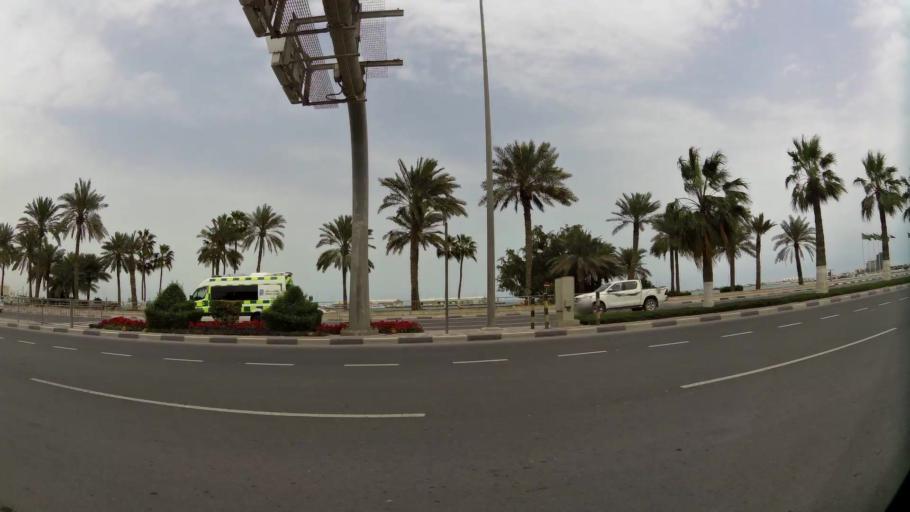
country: QA
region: Baladiyat ad Dawhah
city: Doha
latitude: 25.2900
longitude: 51.5490
